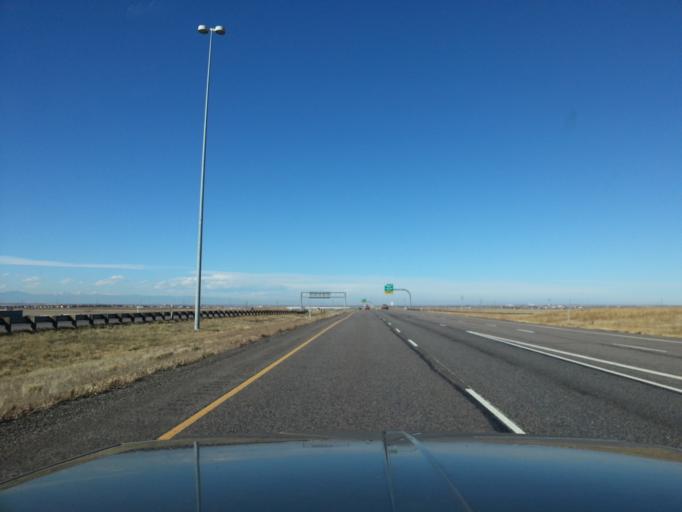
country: US
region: Colorado
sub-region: Adams County
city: Brighton
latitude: 39.8641
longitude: -104.7513
